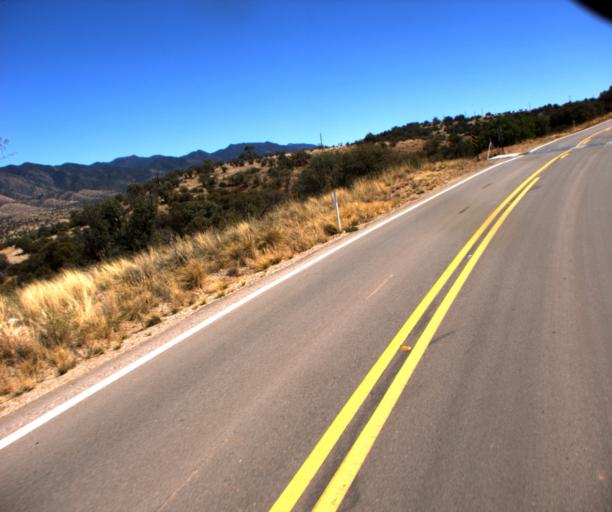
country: US
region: Arizona
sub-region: Cochise County
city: Huachuca City
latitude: 31.5429
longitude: -110.5057
